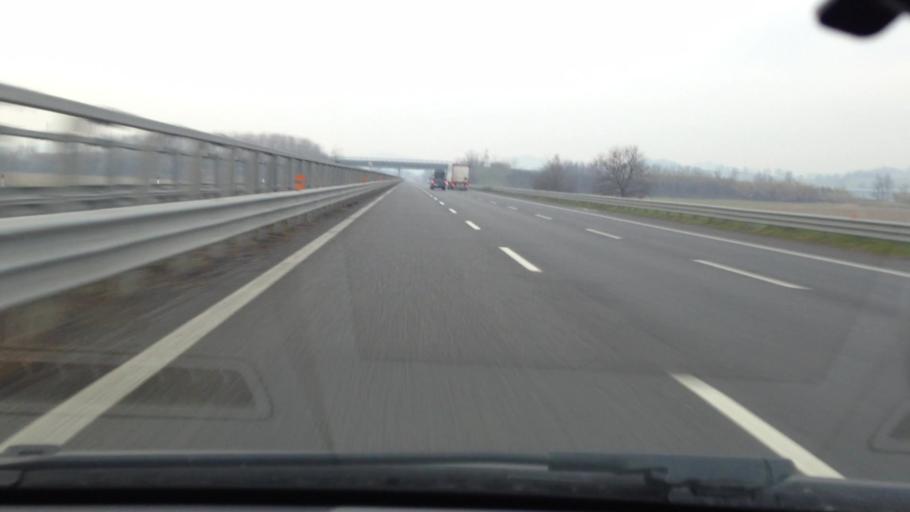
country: IT
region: Piedmont
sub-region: Provincia di Alessandria
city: Castelletto Monferrato
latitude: 44.9550
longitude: 8.5597
